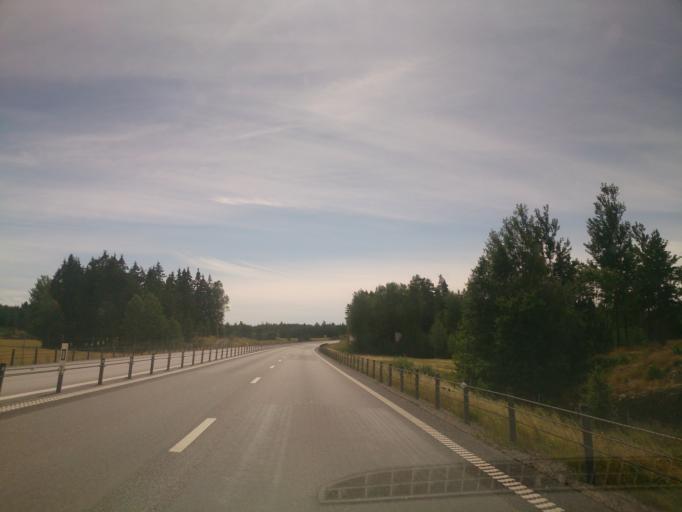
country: SE
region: OEstergoetland
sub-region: Valdemarsviks Kommun
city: Gusum
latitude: 58.3049
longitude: 16.4884
